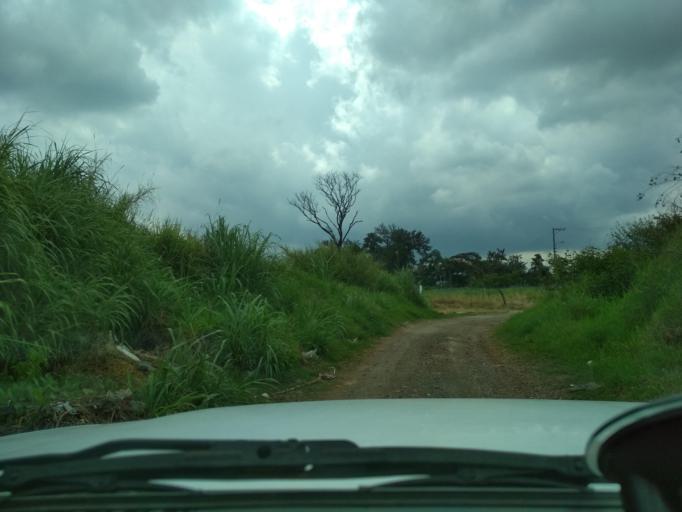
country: MX
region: Veracruz
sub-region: Cordoba
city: San Jose de Abajo [Unidad Habitacional]
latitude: 18.9225
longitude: -96.9597
